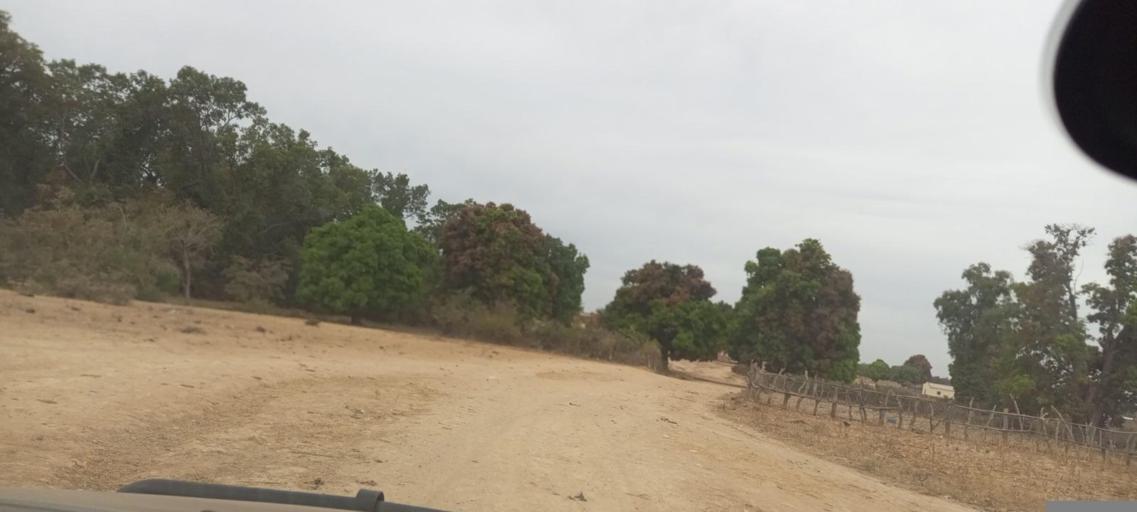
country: ML
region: Koulikoro
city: Kati
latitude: 12.7436
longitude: -8.3308
